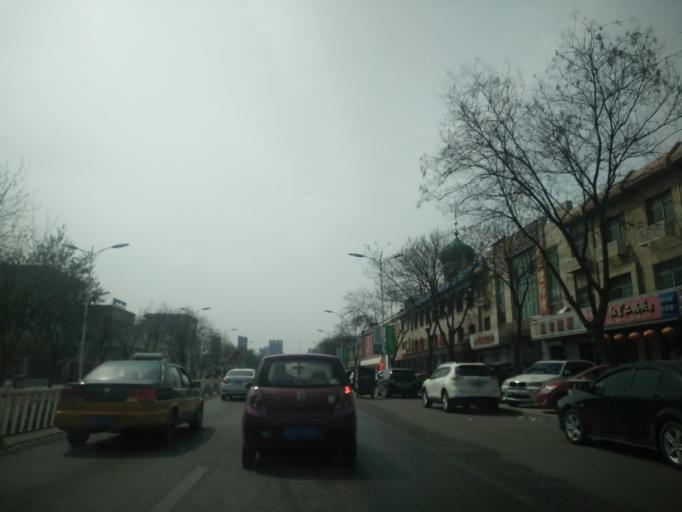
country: CN
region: Beijing
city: Xiji
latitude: 39.7634
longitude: 117.0030
